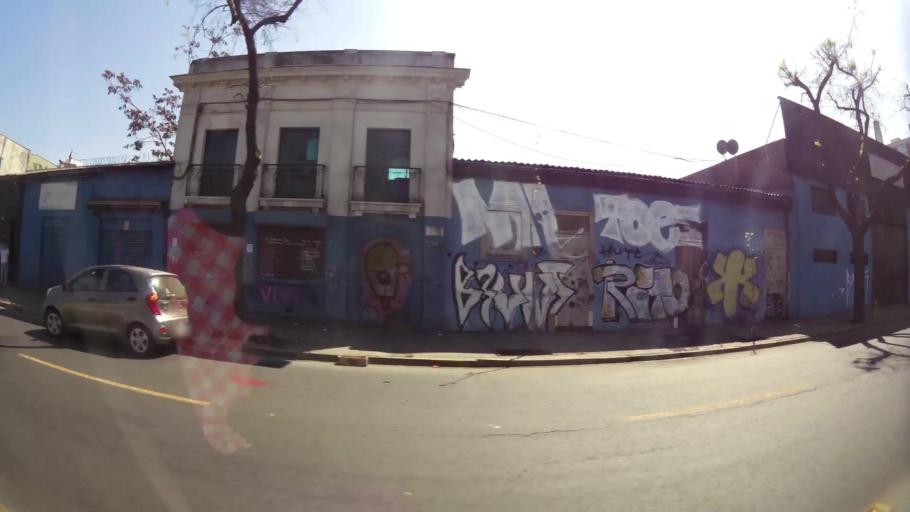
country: CL
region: Santiago Metropolitan
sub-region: Provincia de Santiago
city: Santiago
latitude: -33.4575
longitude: -70.6677
